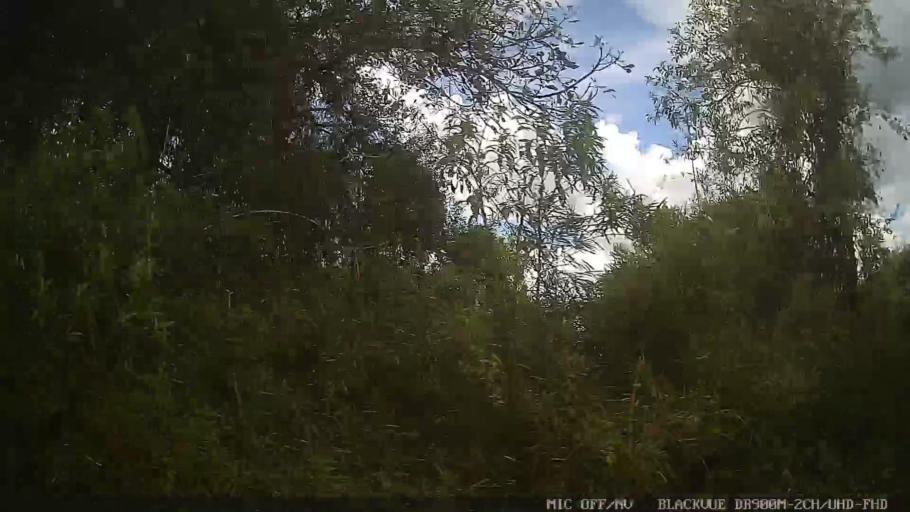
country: BR
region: Sao Paulo
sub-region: Atibaia
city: Atibaia
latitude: -23.1690
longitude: -46.5261
